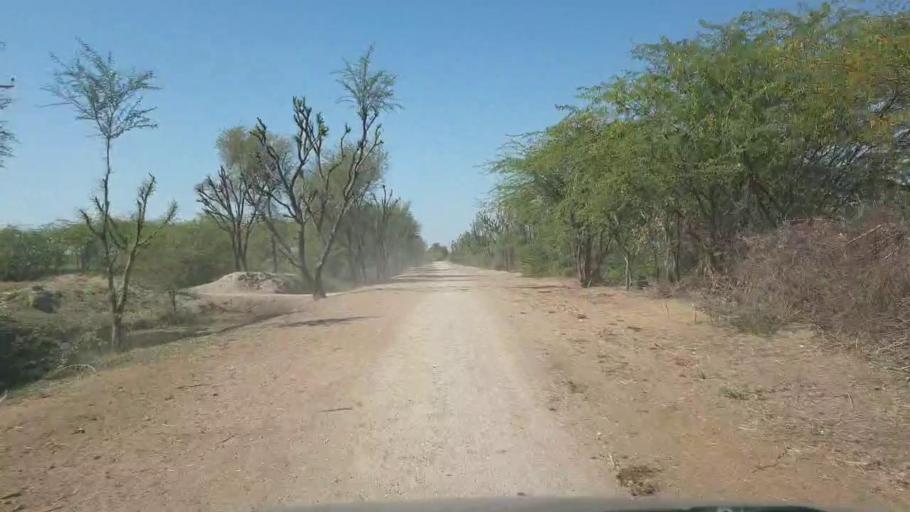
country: PK
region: Sindh
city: Dhoro Naro
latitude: 25.4305
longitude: 69.6138
